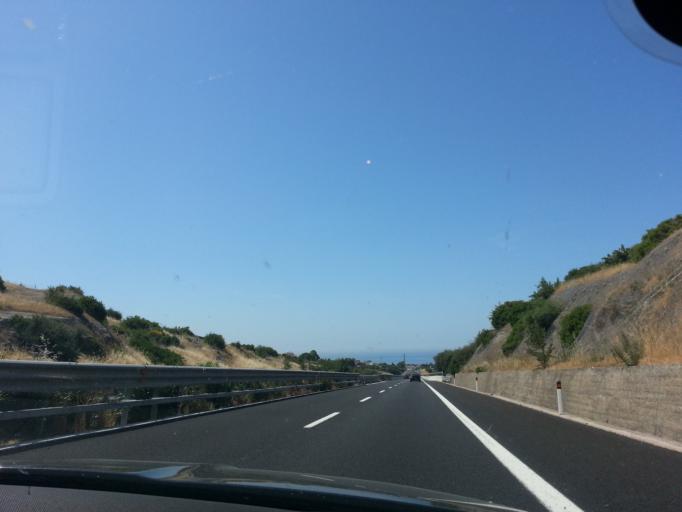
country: IT
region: Latium
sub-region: Citta metropolitana di Roma Capitale
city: Civitavecchia
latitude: 42.0869
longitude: 11.8280
